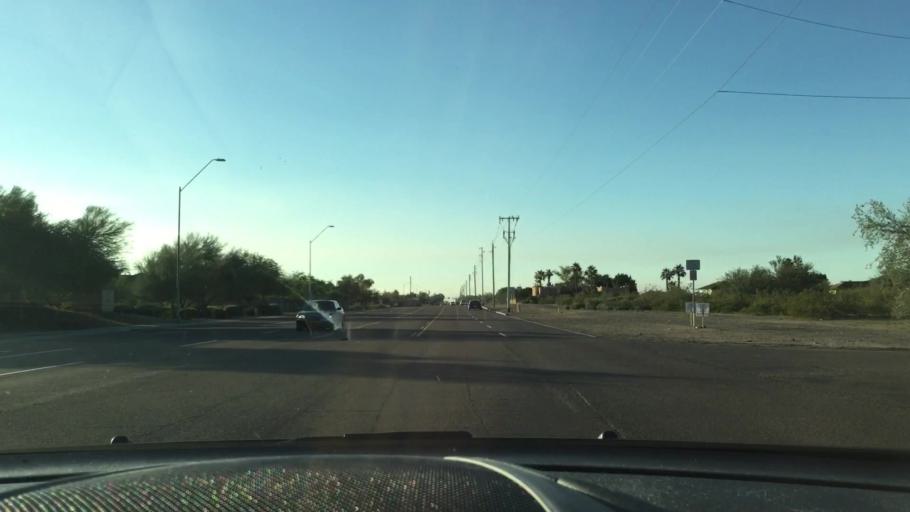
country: US
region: Arizona
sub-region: Maricopa County
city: Sun City
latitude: 33.7036
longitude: -112.2032
